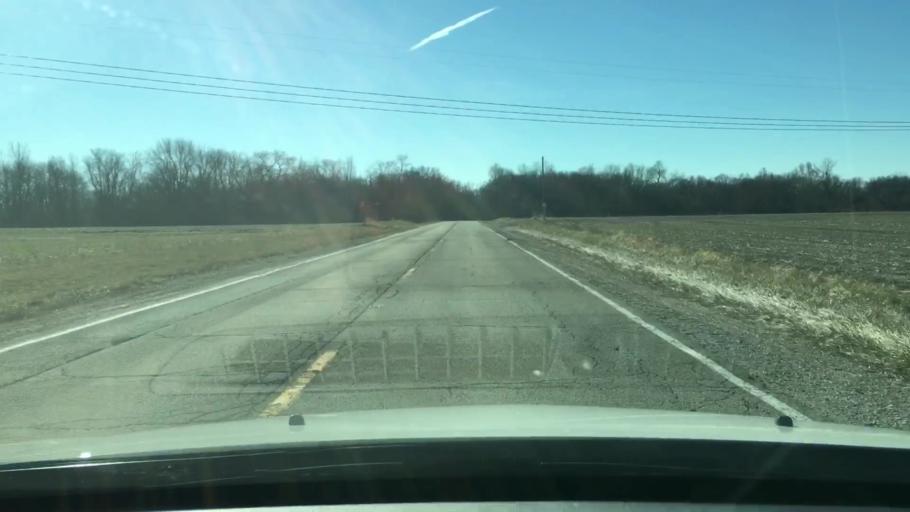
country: US
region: Illinois
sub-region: Mason County
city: Havana
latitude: 40.2908
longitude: -90.1555
